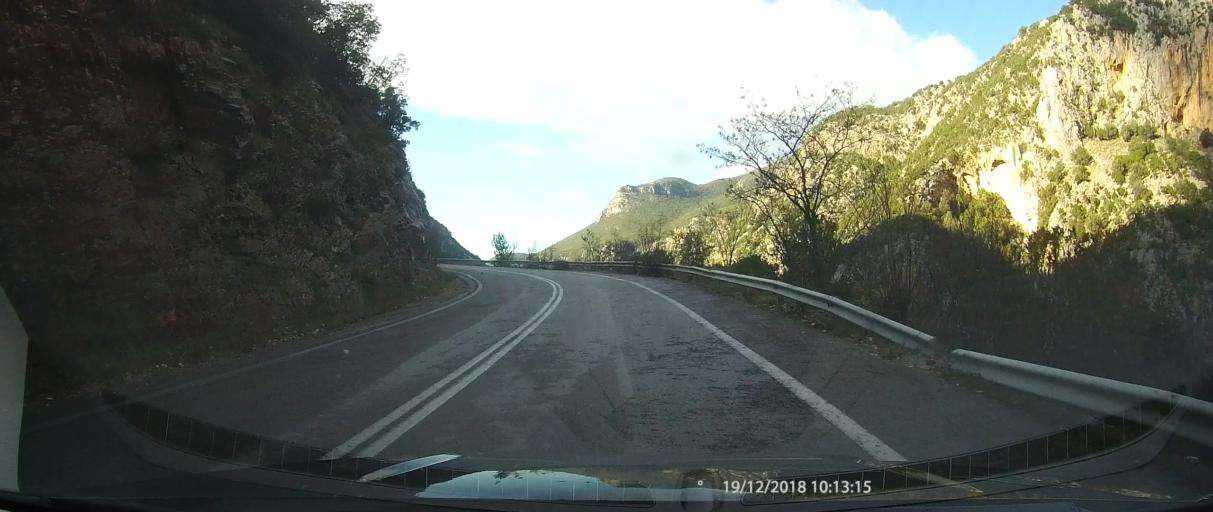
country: GR
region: Peloponnese
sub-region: Nomos Messinias
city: Kalamata
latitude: 37.0871
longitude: 22.1615
